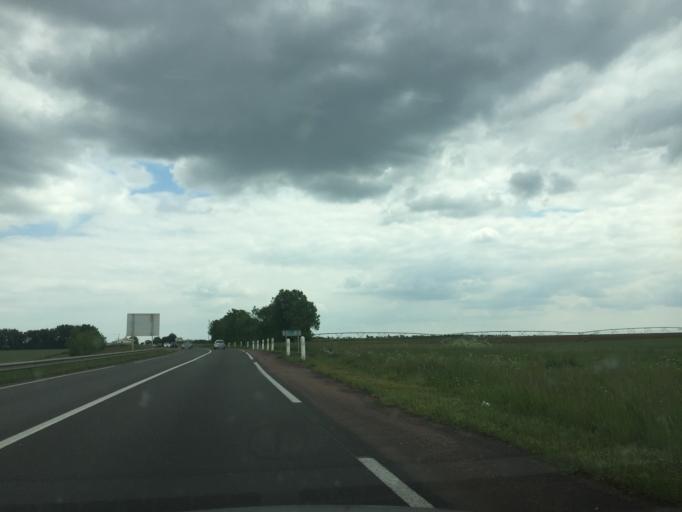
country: FR
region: Pays de la Loire
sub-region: Departement de la Vendee
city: Benet
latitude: 46.3904
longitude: -0.6349
